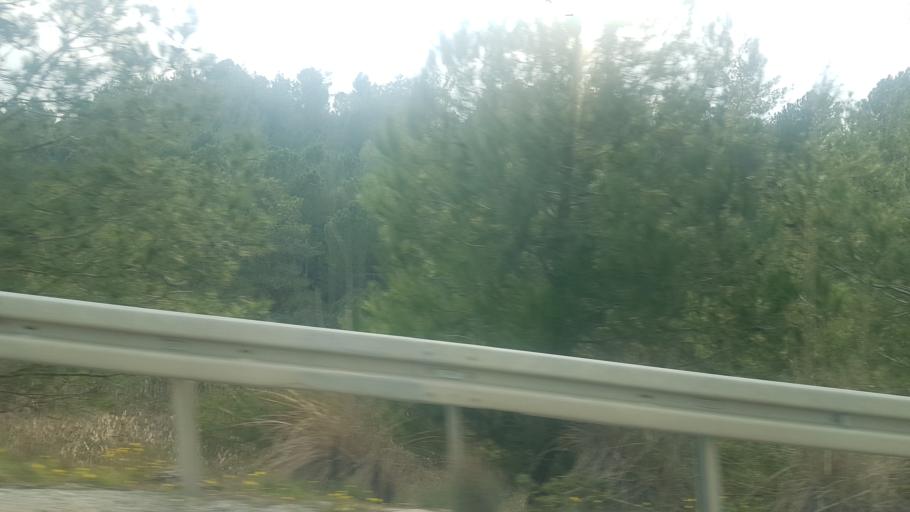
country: TR
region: Mersin
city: Yenice
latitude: 37.0848
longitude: 35.1731
